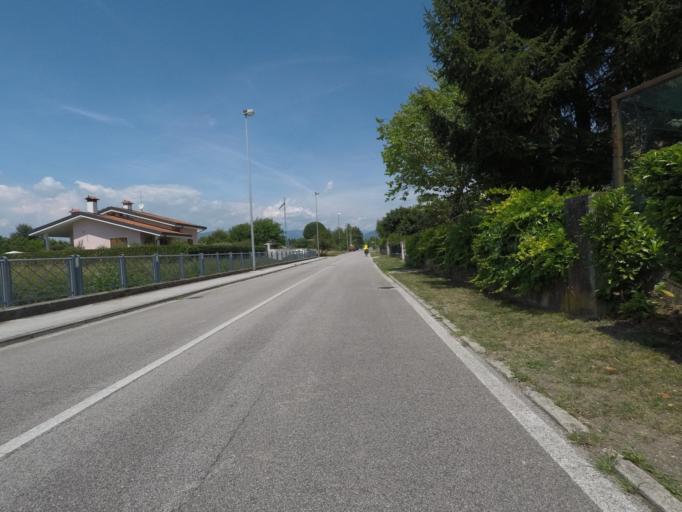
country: IT
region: Friuli Venezia Giulia
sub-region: Provincia di Pordenone
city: Spilimbergo
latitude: 46.1200
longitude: 12.9021
